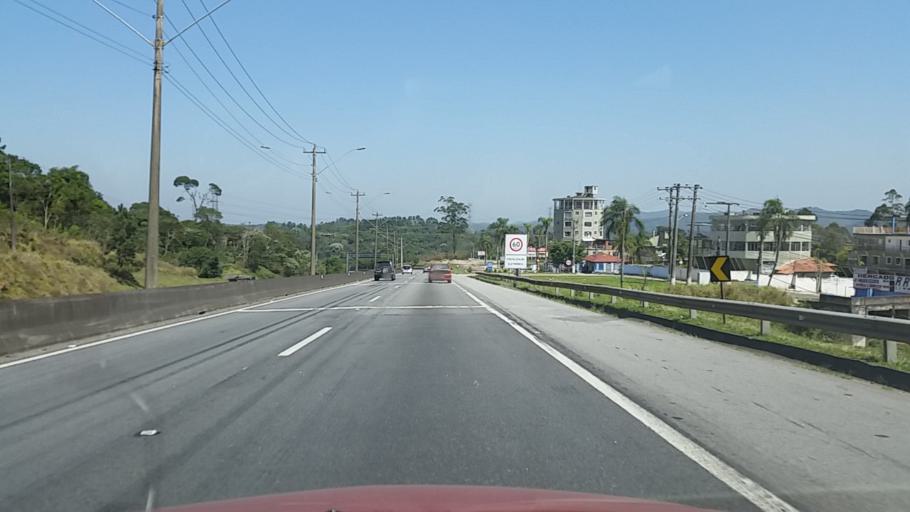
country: BR
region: Sao Paulo
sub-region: Sao Lourenco Da Serra
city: Sao Lourenco da Serra
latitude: -23.8044
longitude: -46.9219
